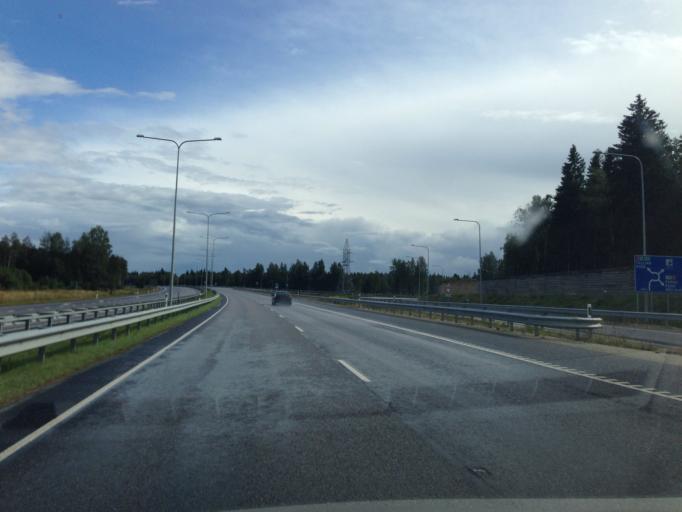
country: EE
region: Jaervamaa
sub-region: Paide linn
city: Paide
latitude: 58.9027
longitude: 25.6356
